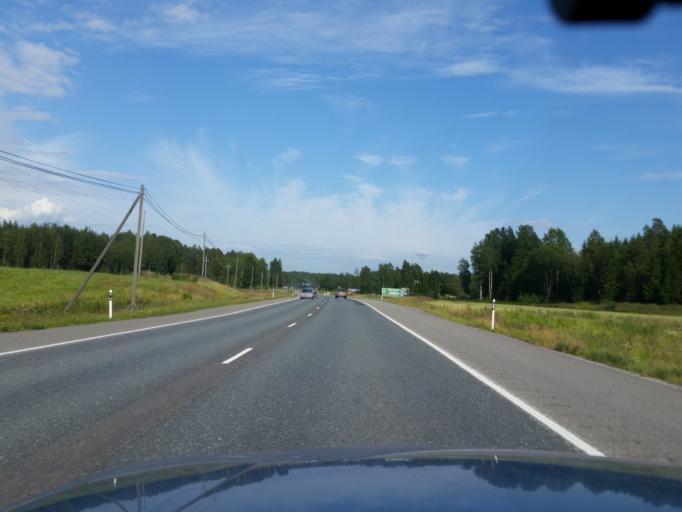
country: FI
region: Uusimaa
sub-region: Helsinki
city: Siuntio
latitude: 60.0932
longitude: 24.2338
